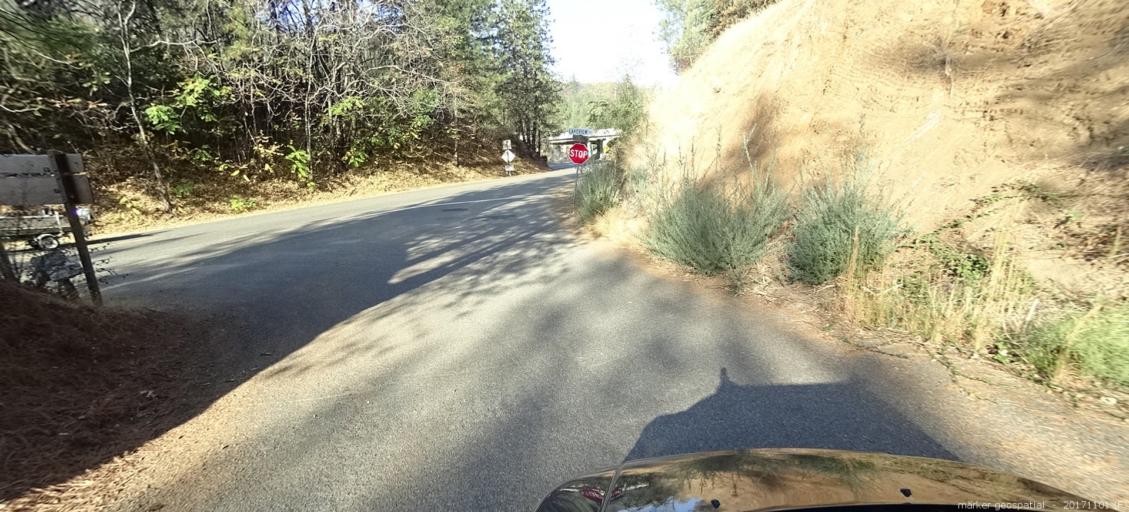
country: US
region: California
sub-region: Shasta County
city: Shasta Lake
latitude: 40.8064
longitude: -122.3207
